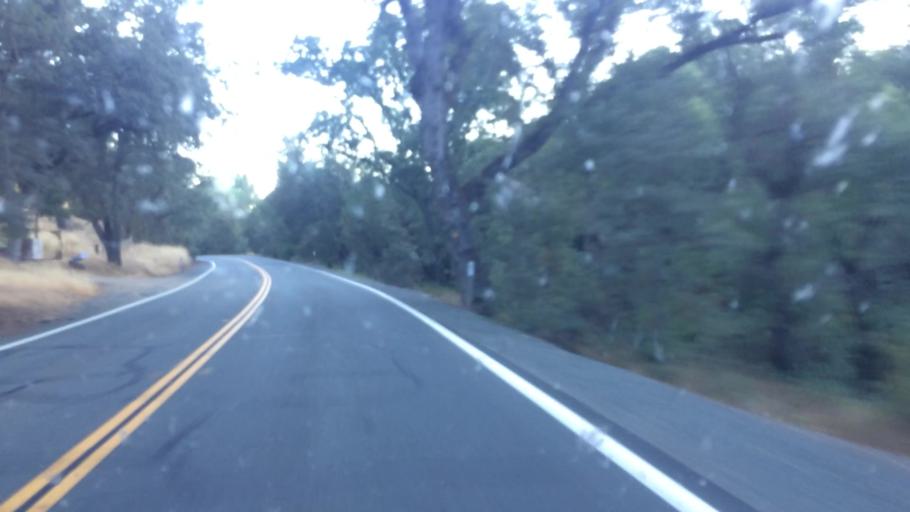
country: US
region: California
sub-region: Amador County
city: Plymouth
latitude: 38.5458
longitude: -120.8479
